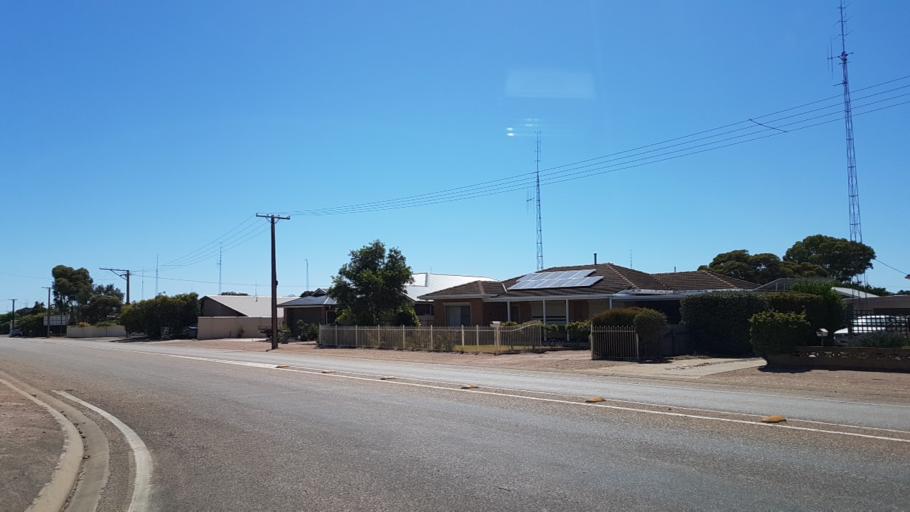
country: AU
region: South Australia
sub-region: Copper Coast
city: Kadina
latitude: -33.9667
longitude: 137.7225
